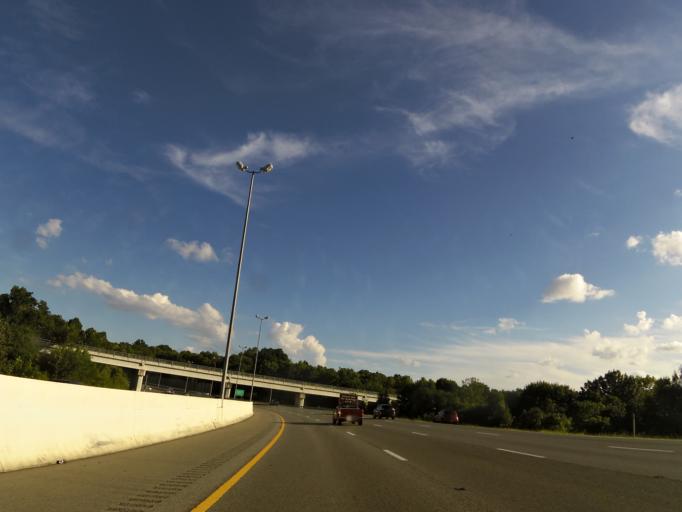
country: US
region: Tennessee
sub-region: Davidson County
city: Lakewood
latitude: 36.1806
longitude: -86.6961
